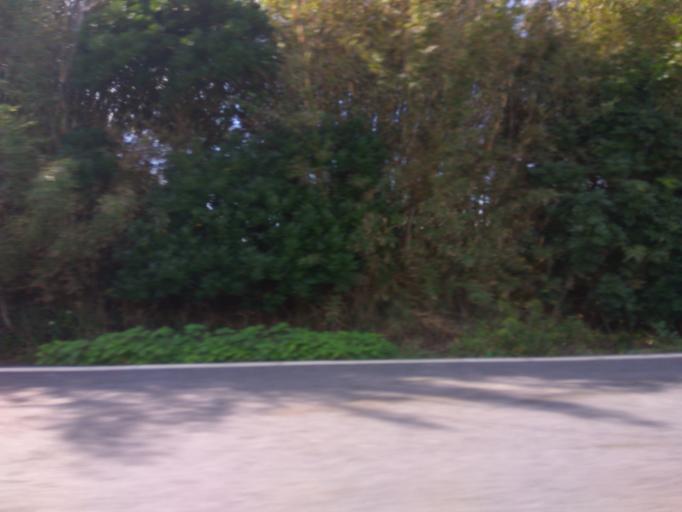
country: TW
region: Taiwan
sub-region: Hsinchu
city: Zhubei
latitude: 25.0133
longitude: 121.0744
